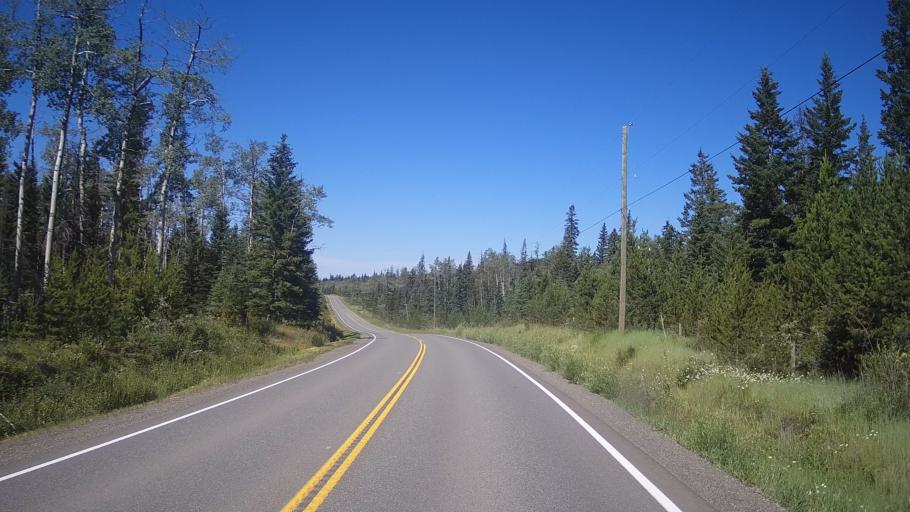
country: CA
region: British Columbia
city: Cache Creek
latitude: 51.5474
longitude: -121.0790
